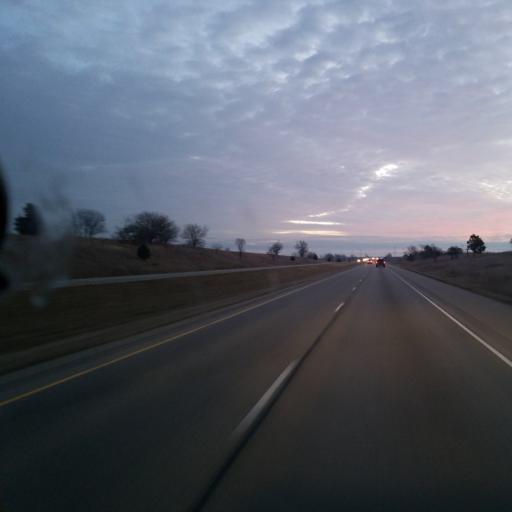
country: US
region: Illinois
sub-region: Tazewell County
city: Morton
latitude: 40.6213
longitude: -89.4186
